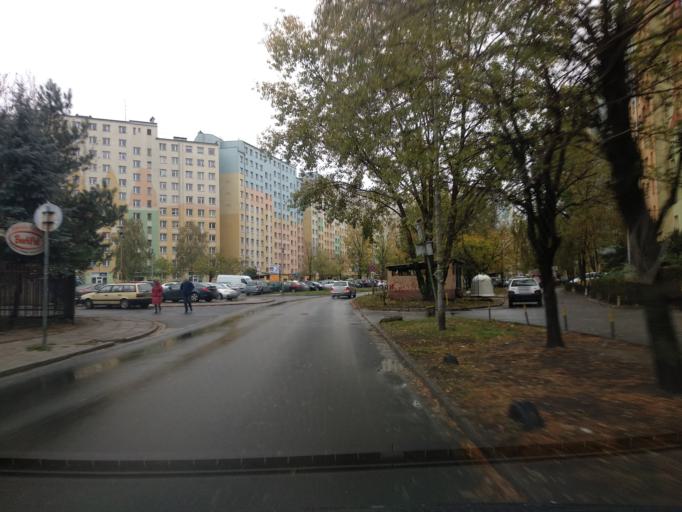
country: PL
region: Lower Silesian Voivodeship
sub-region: Powiat wroclawski
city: Wroclaw
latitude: 51.0821
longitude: 17.0408
